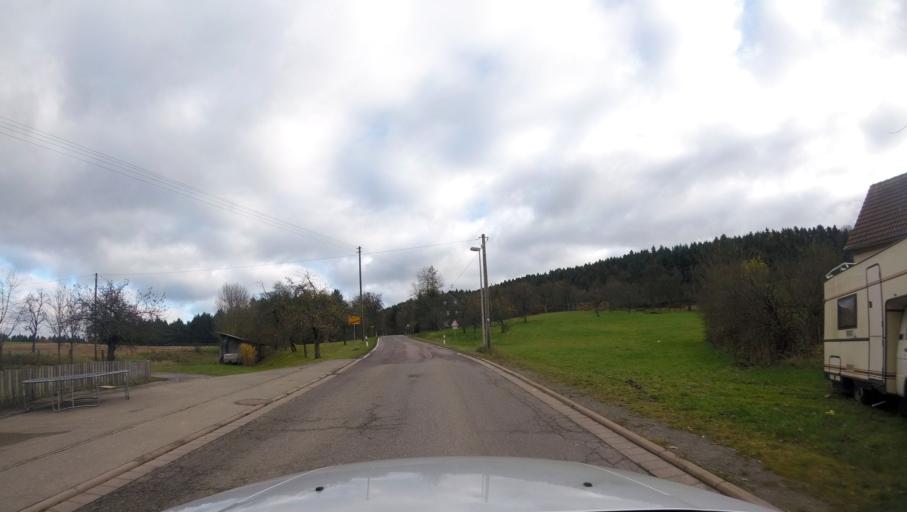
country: DE
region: Baden-Wuerttemberg
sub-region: Regierungsbezirk Stuttgart
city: Fichtenberg
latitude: 48.9494
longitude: 9.6864
